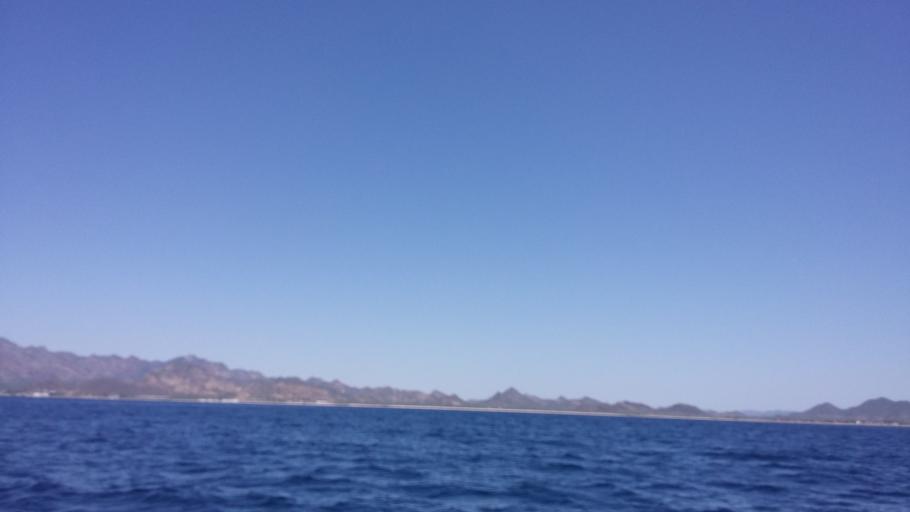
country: MX
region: Sonora
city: Heroica Guaymas
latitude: 27.9266
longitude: -111.0022
